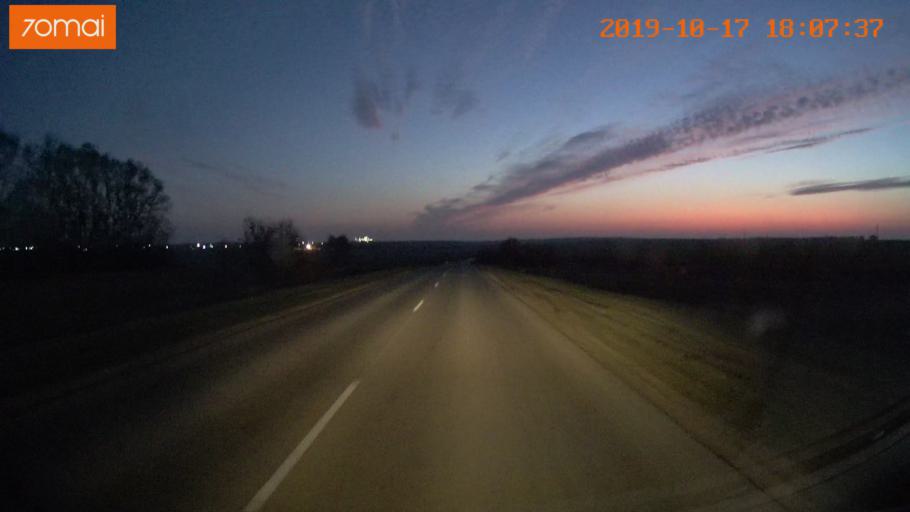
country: RU
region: Tula
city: Kurkino
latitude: 53.4423
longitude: 38.6522
